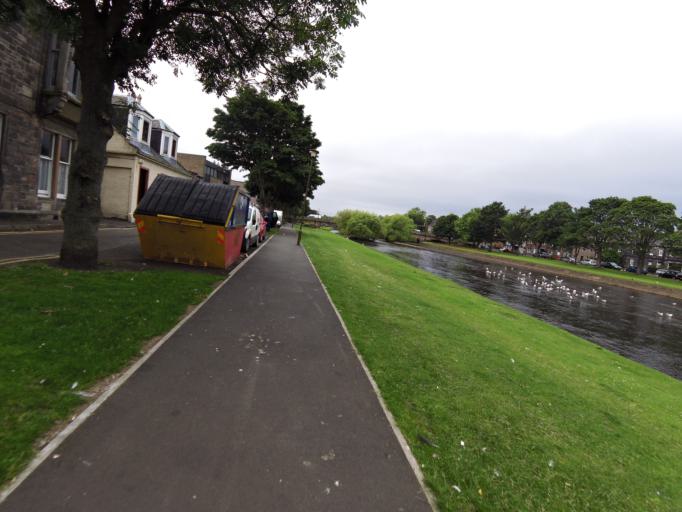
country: GB
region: Scotland
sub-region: East Lothian
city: Musselburgh
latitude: 55.9431
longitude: -3.0525
